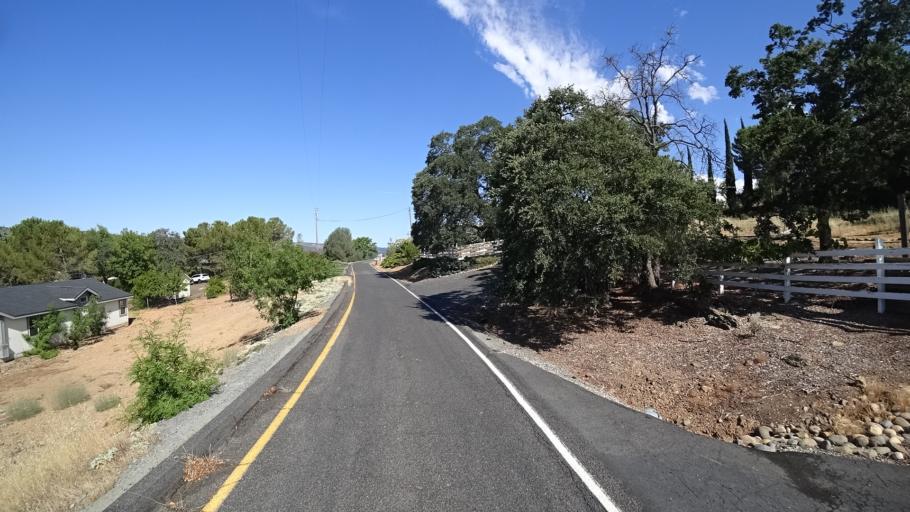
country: US
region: California
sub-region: Calaveras County
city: Copperopolis
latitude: 37.9270
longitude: -120.6346
